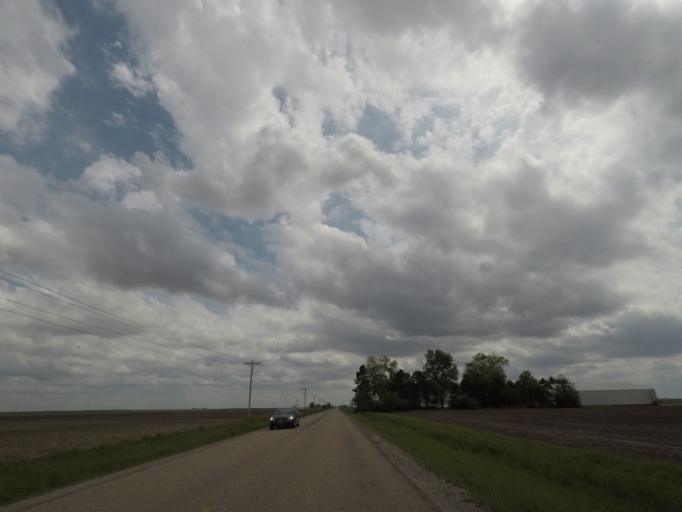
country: US
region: Illinois
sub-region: Macon County
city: Maroa
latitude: 40.0831
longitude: -89.0859
